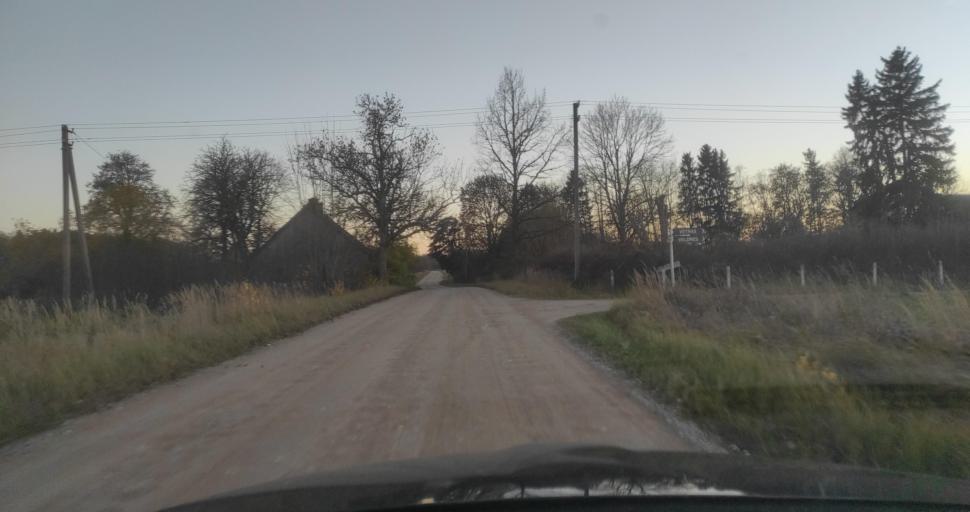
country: LV
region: Saldus Rajons
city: Saldus
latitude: 56.8049
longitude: 22.2849
